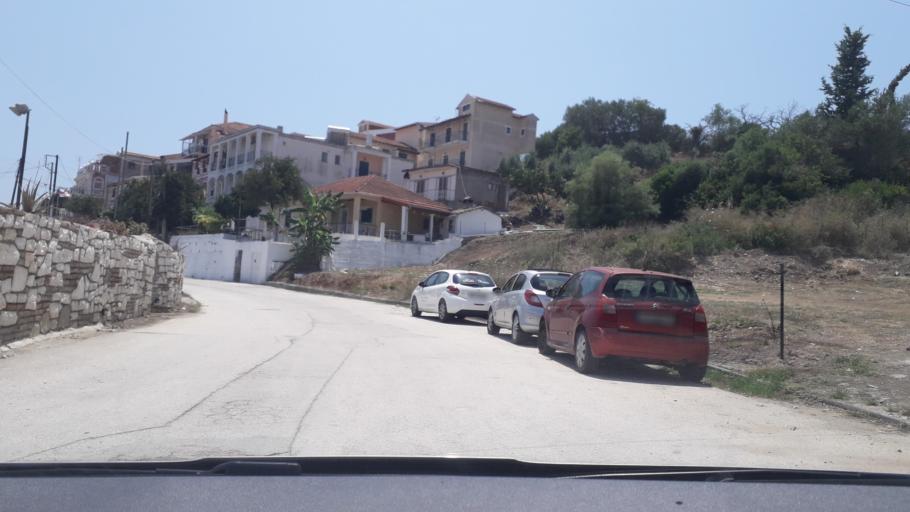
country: GR
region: Ionian Islands
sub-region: Nomos Kerkyras
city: Lefkimmi
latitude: 39.3822
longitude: 20.1140
